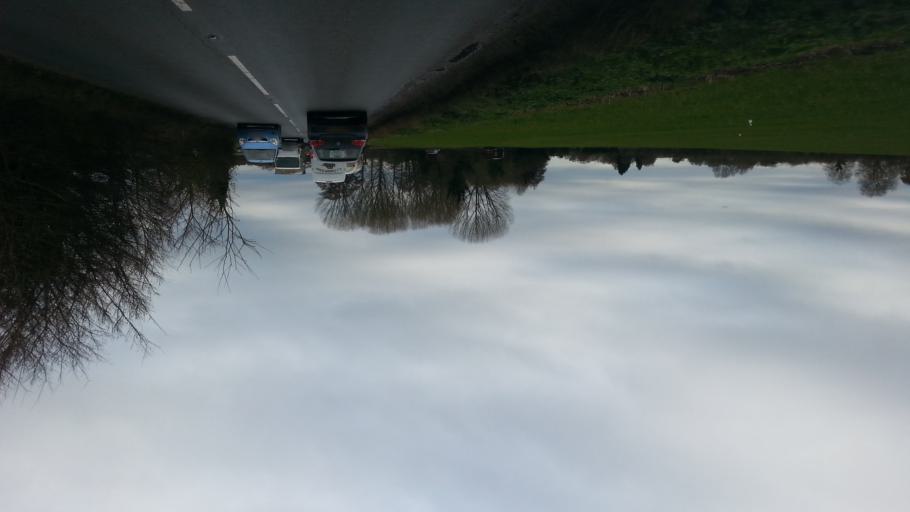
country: GB
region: England
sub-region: Norfolk
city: Diss
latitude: 52.3561
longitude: 1.1953
